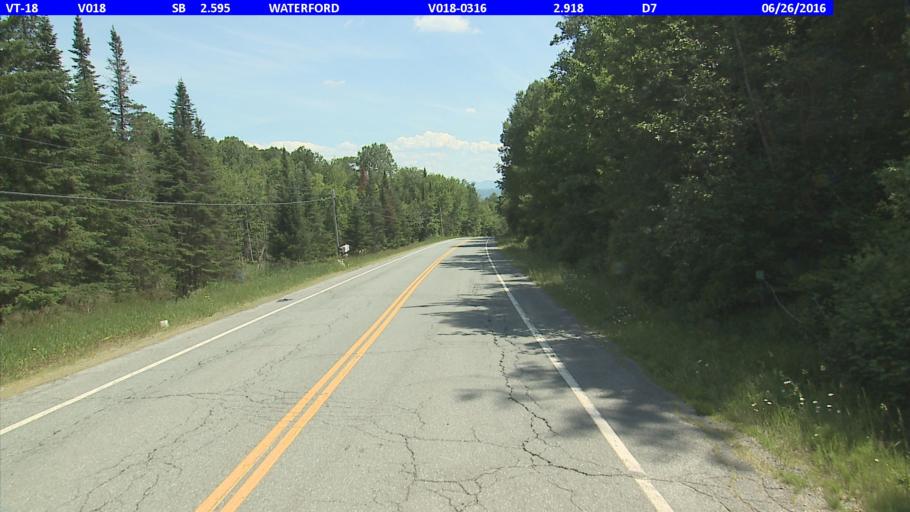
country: US
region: Vermont
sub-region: Caledonia County
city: Saint Johnsbury
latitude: 44.3734
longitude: -71.9103
